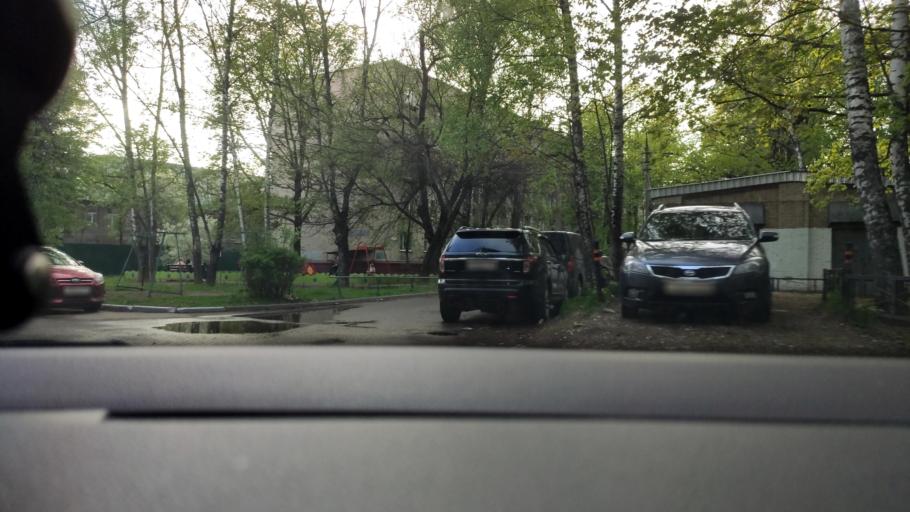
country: RU
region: Moscow
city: Khimki
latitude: 55.8961
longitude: 37.4428
